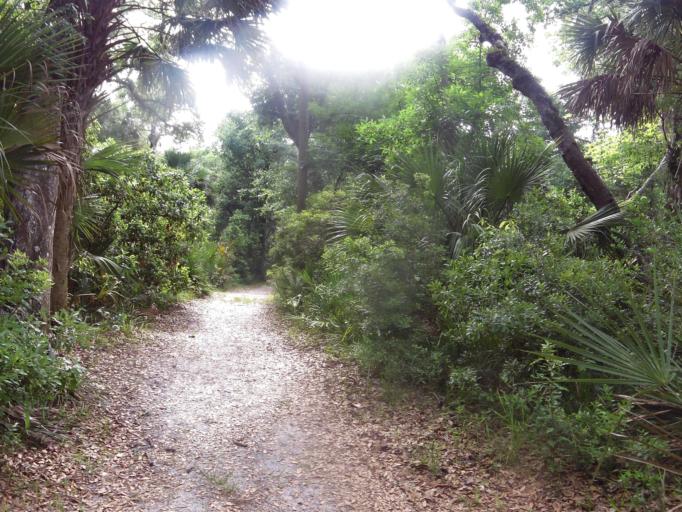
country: US
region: Florida
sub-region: Flagler County
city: Palm Coast
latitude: 29.6365
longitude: -81.2078
